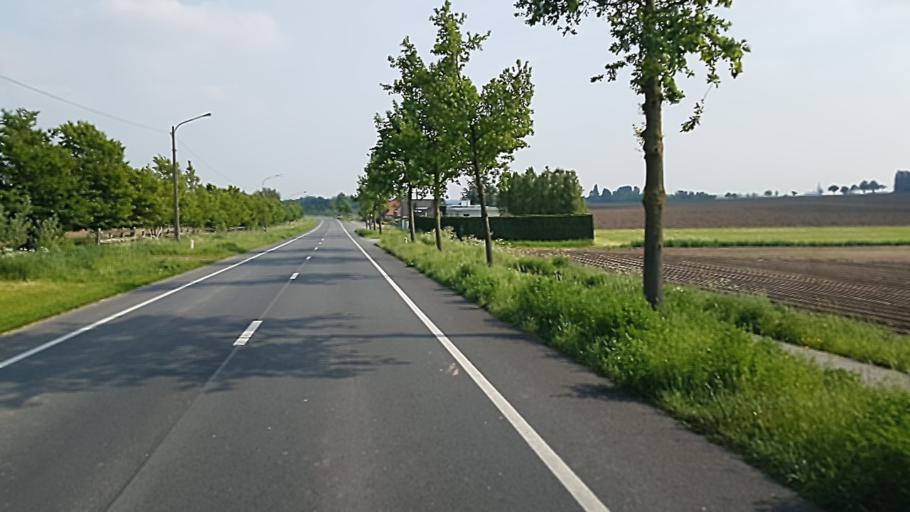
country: BE
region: Flanders
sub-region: Provincie West-Vlaanderen
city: Zwevegem
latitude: 50.7541
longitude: 3.3141
